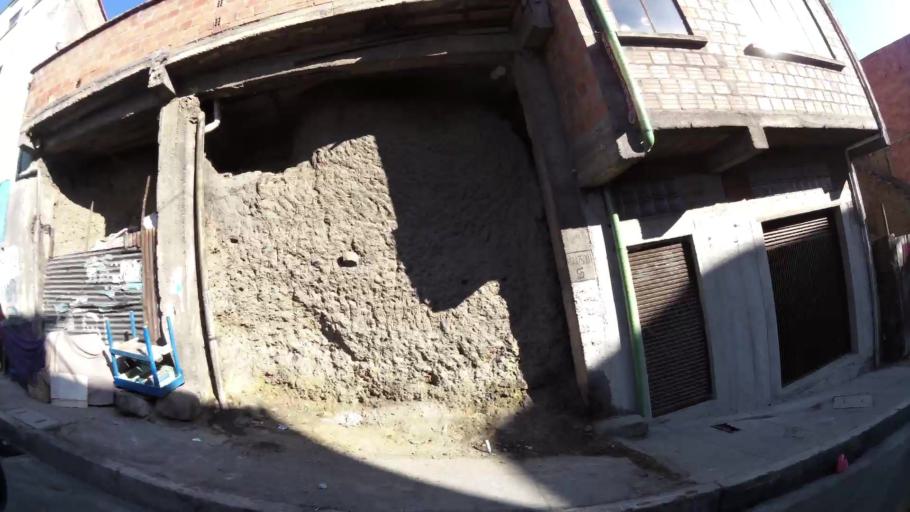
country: BO
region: La Paz
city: La Paz
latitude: -16.5033
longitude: -68.1514
